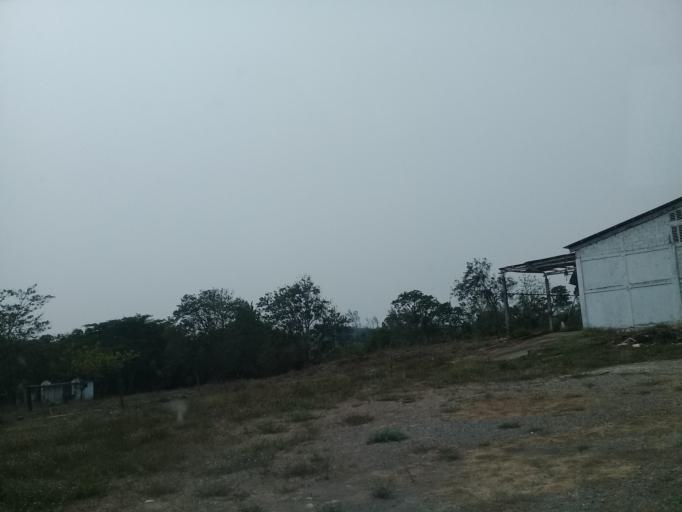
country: MX
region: Veracruz
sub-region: Medellin
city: La Laguna y Monte del Castillo
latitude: 18.9824
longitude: -96.1199
